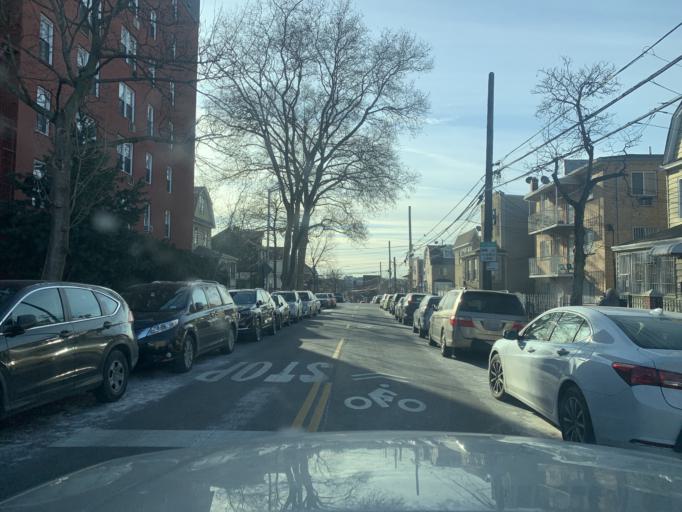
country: US
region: New York
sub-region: Queens County
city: Long Island City
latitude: 40.7422
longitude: -73.8907
